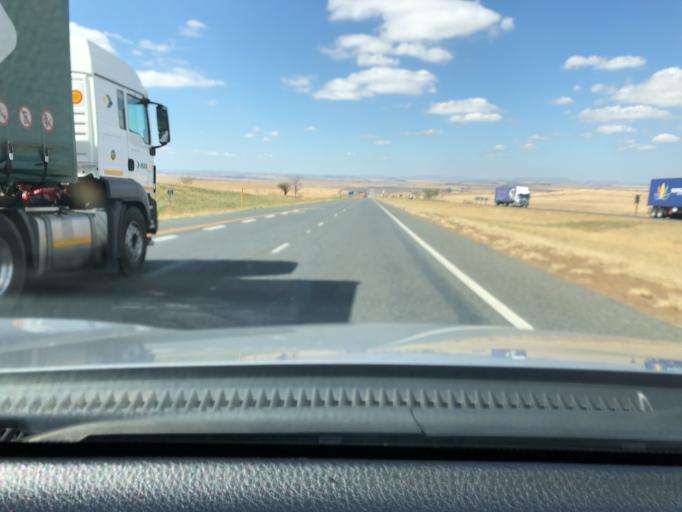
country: ZA
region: KwaZulu-Natal
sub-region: uThukela District Municipality
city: Estcourt
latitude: -28.8857
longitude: 29.7484
